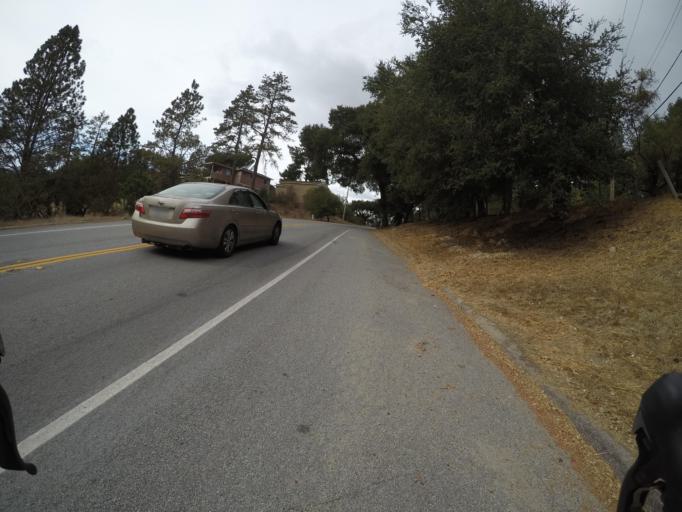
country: US
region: California
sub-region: Santa Cruz County
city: Ben Lomond
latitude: 37.0845
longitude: -122.0679
